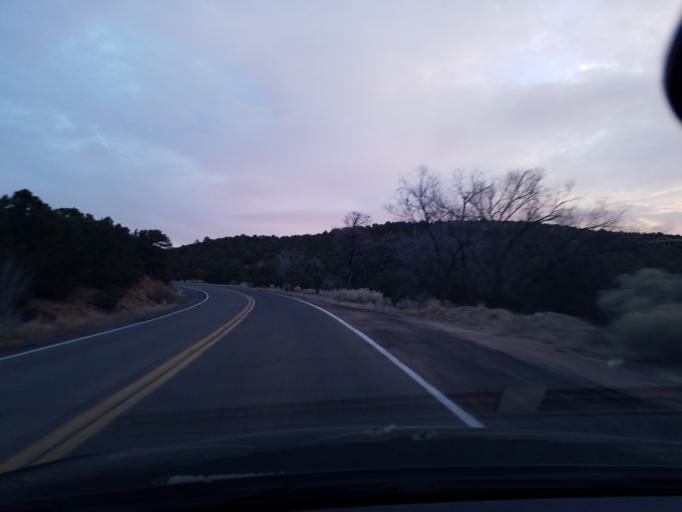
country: US
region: New Mexico
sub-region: Santa Fe County
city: Santa Fe
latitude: 35.7066
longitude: -105.9010
